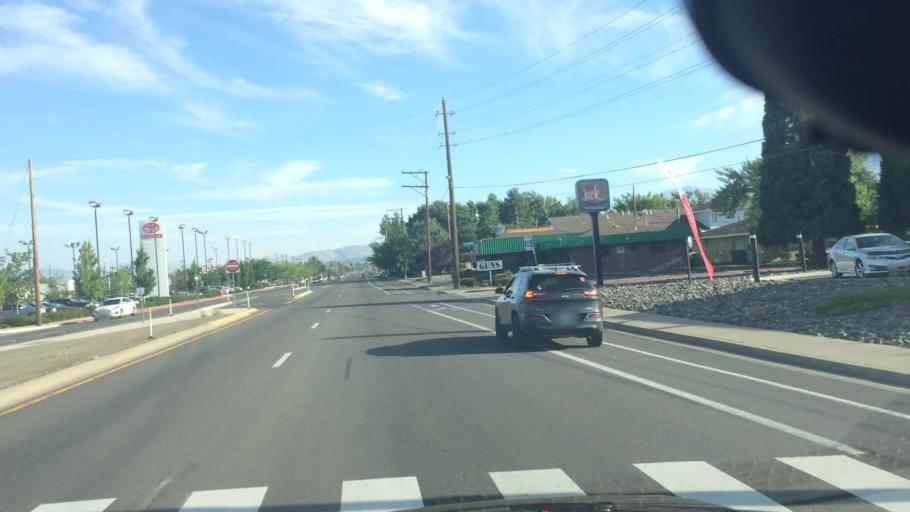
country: US
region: Nevada
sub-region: Washoe County
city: Reno
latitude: 39.5043
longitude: -119.7892
